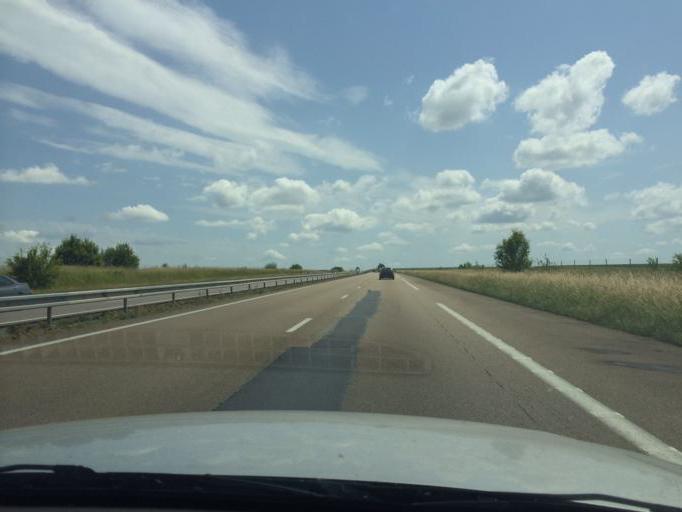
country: FR
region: Champagne-Ardenne
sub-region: Departement de la Marne
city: Mourmelon-le-Grand
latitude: 49.0825
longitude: 4.2618
